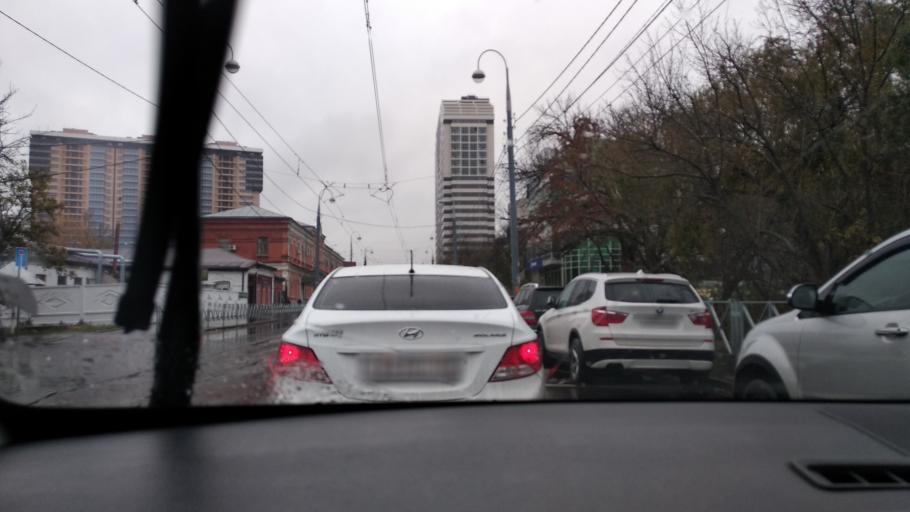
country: RU
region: Krasnodarskiy
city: Krasnodar
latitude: 45.0262
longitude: 38.9908
